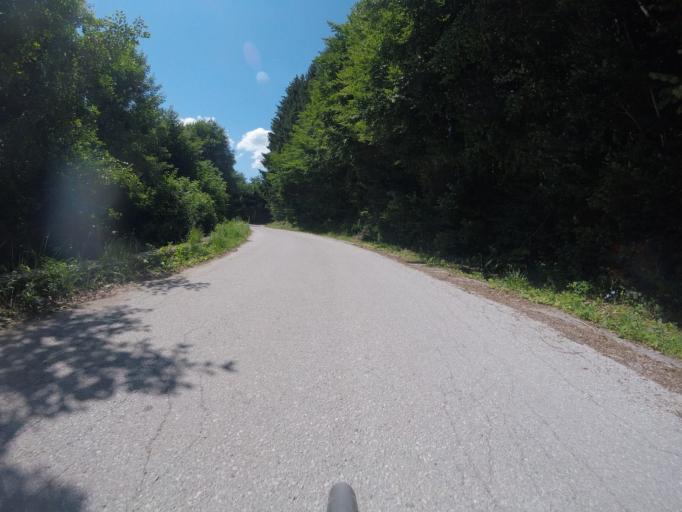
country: SI
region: Kostanjevica na Krki
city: Kostanjevica na Krki
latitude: 45.7825
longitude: 15.4785
